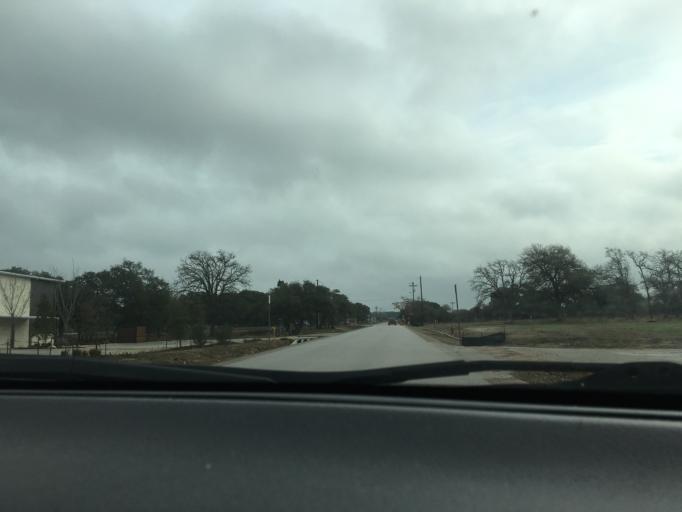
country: US
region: Texas
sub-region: Hays County
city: Dripping Springs
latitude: 30.1852
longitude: -98.0843
